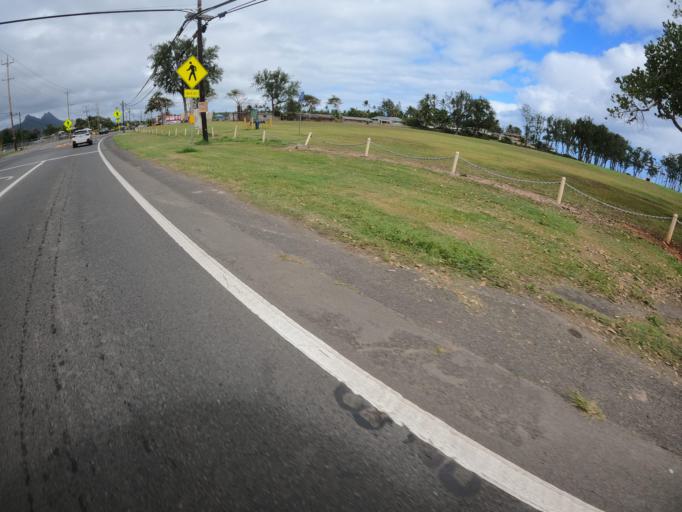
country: US
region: Hawaii
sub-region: Honolulu County
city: Waimanalo Beach
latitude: 21.3319
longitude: -157.6963
